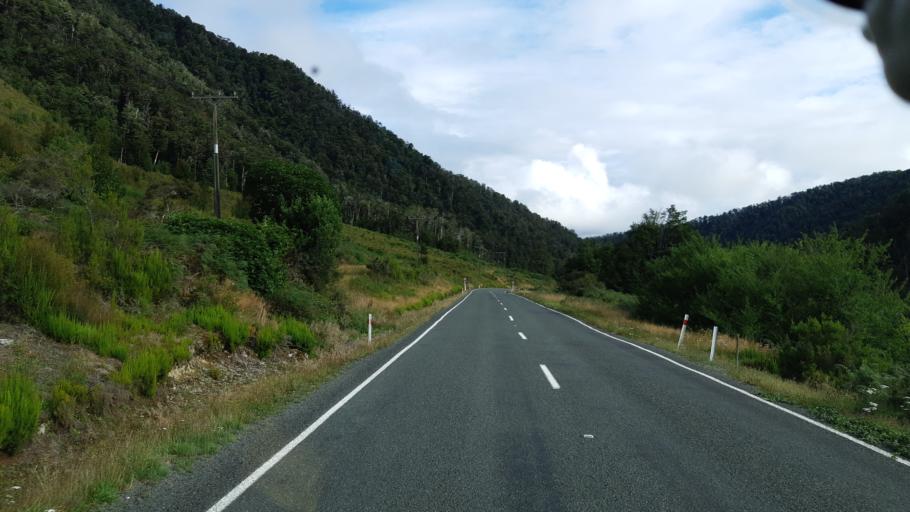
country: NZ
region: West Coast
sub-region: Buller District
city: Westport
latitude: -42.0011
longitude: 172.2279
